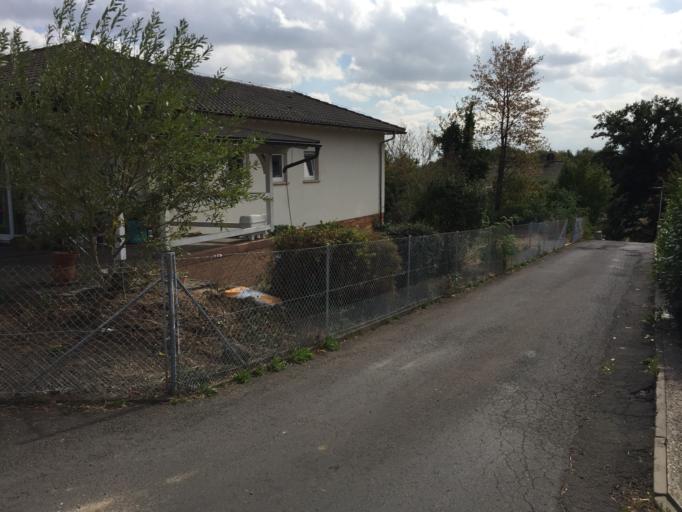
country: DE
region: Hesse
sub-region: Regierungsbezirk Darmstadt
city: Wolfersheim
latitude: 50.4538
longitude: 8.8305
